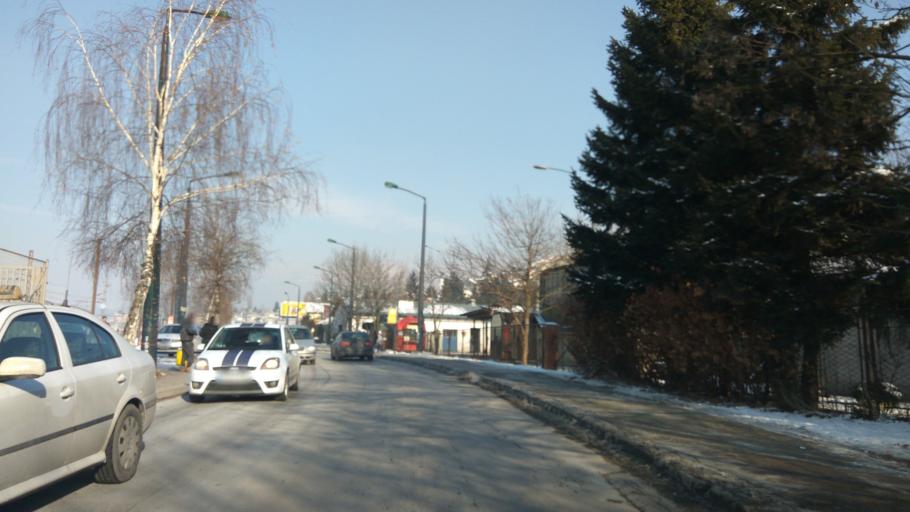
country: BA
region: Federation of Bosnia and Herzegovina
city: Kobilja Glava
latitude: 43.8617
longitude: 18.4012
